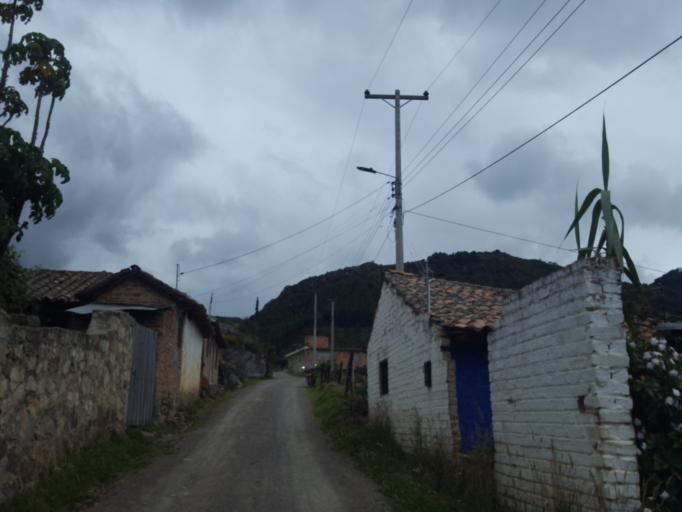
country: CO
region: Boyaca
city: Mongui
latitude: 5.7146
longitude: -72.8479
